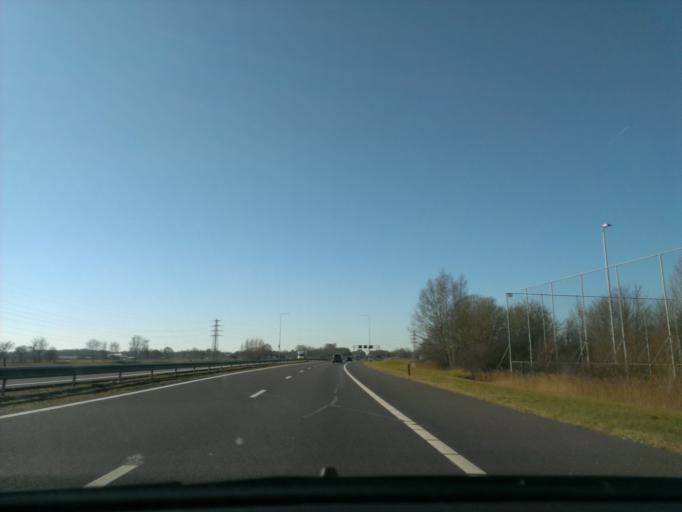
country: NL
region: Drenthe
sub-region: Gemeente Meppel
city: Meppel
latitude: 52.6862
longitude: 6.2033
